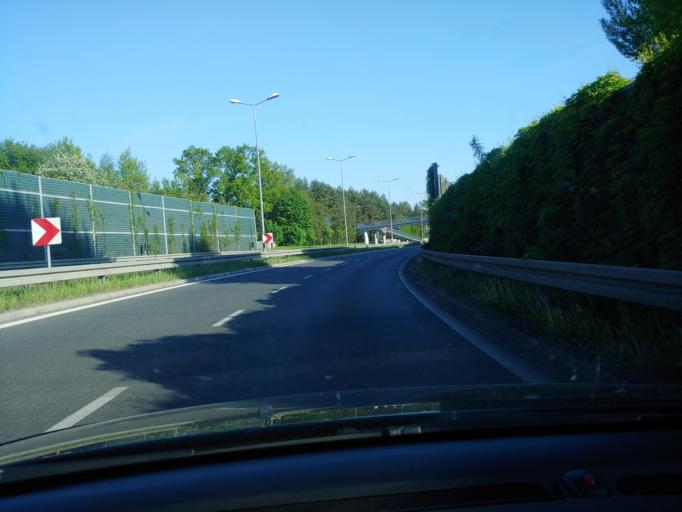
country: PL
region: Silesian Voivodeship
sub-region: Jaworzno
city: Jaworzno
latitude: 50.1846
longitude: 19.2886
